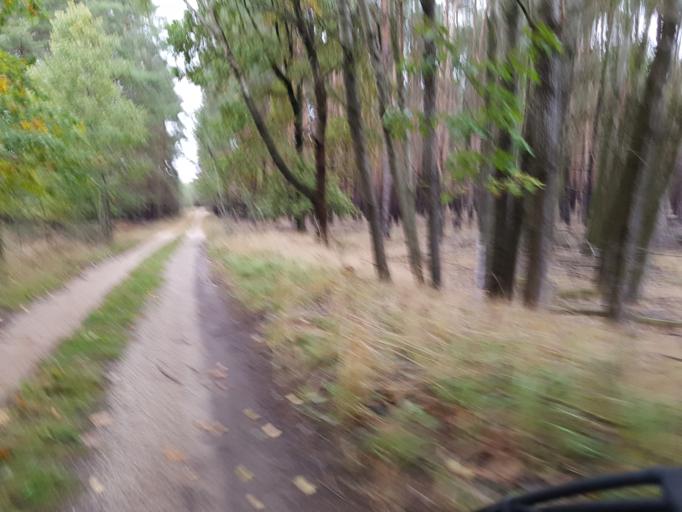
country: DE
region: Brandenburg
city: Schilda
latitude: 51.6156
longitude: 13.3929
